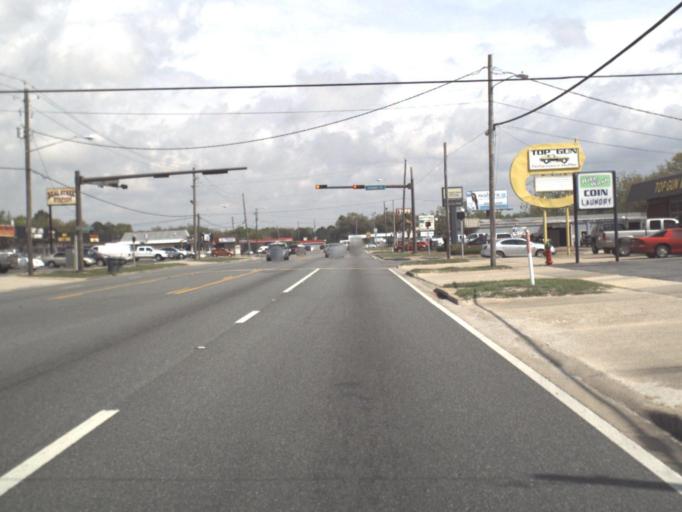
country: US
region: Florida
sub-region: Okaloosa County
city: Fort Walton Beach
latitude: 30.4192
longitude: -86.6136
